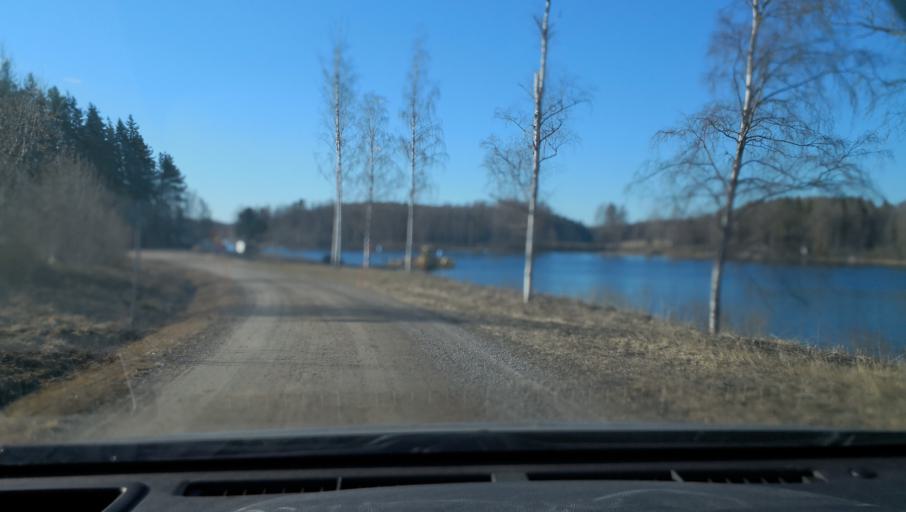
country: SE
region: Dalarna
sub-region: Avesta Kommun
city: Horndal
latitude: 60.1818
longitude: 16.6265
